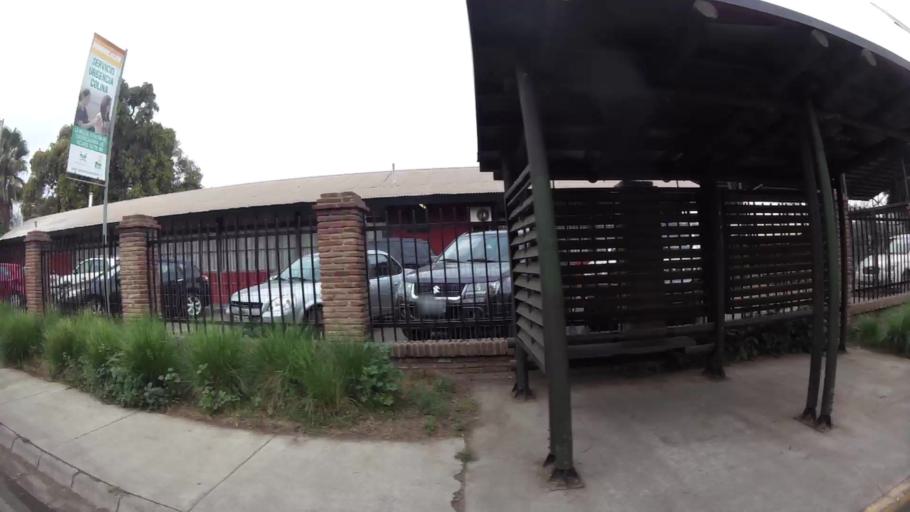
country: CL
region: Santiago Metropolitan
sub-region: Provincia de Chacabuco
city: Chicureo Abajo
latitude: -33.2433
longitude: -70.6798
